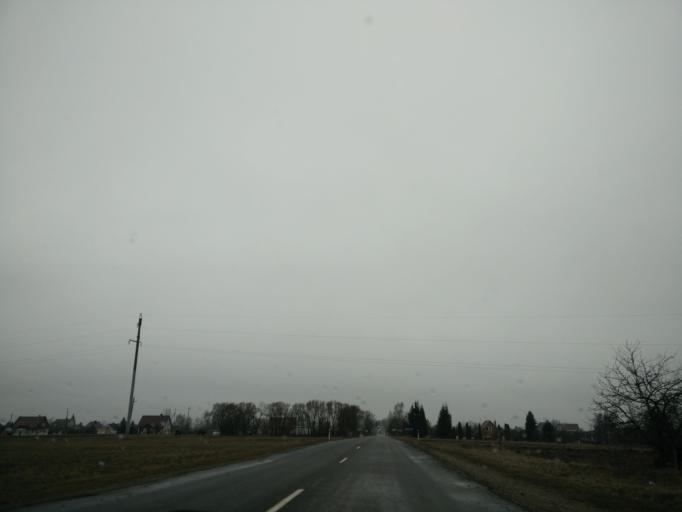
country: LT
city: Ariogala
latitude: 55.3564
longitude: 23.3756
